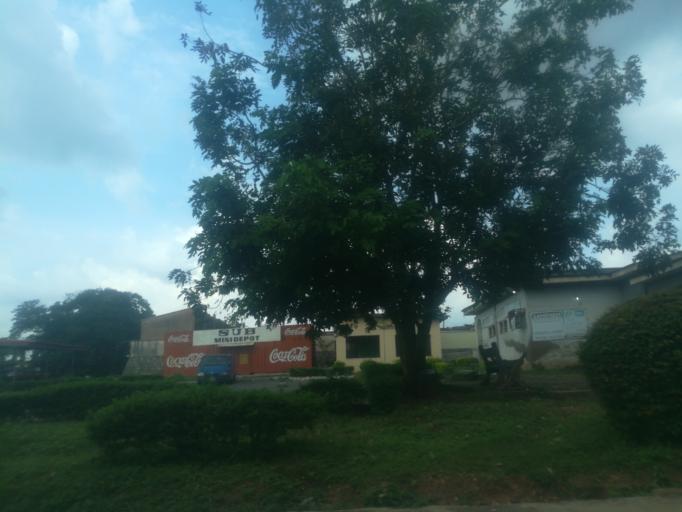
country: NG
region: Oyo
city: Ibadan
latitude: 7.4441
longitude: 3.8976
